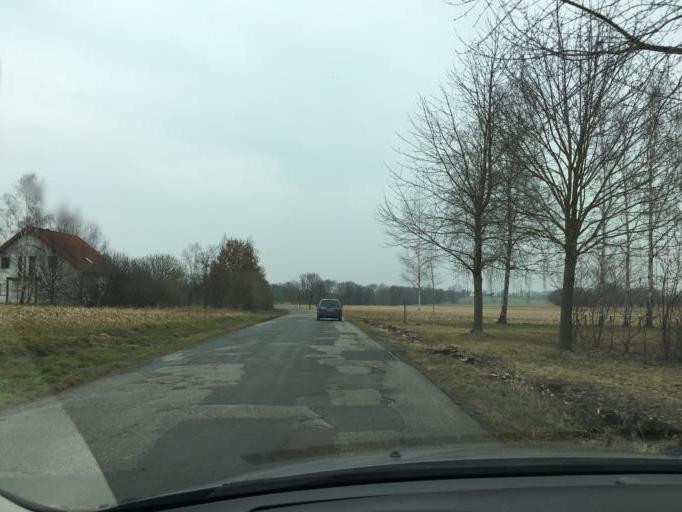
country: DE
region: Thuringia
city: Gerstenberg
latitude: 51.0336
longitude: 12.4388
